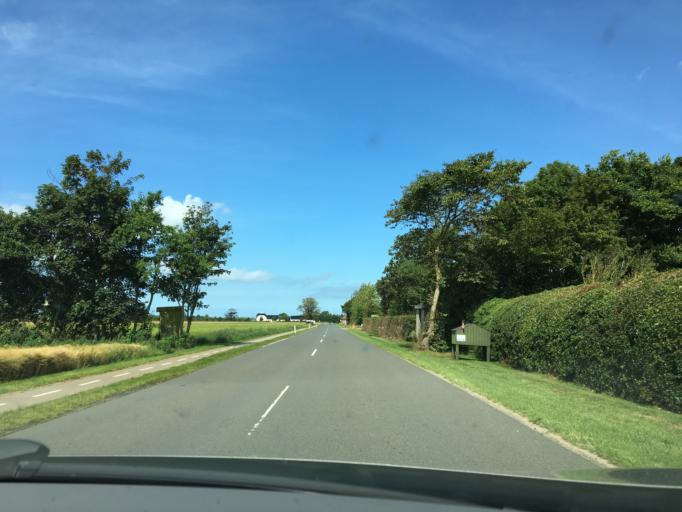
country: DK
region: Central Jutland
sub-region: Ringkobing-Skjern Kommune
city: Skjern
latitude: 55.9512
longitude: 8.4067
